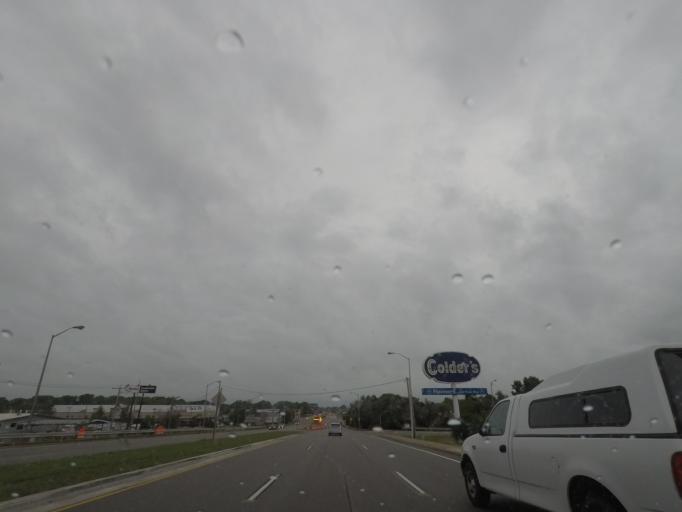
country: US
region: Wisconsin
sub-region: Waukesha County
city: Elm Grove
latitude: 43.0266
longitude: -88.0473
